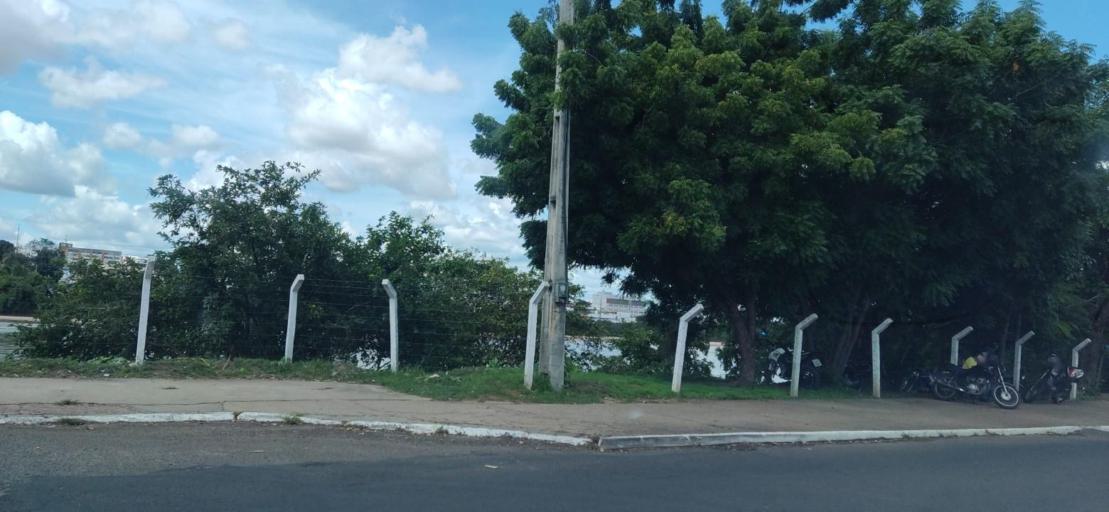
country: BR
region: Maranhao
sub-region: Timon
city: Timon
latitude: -5.0935
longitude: -42.8221
